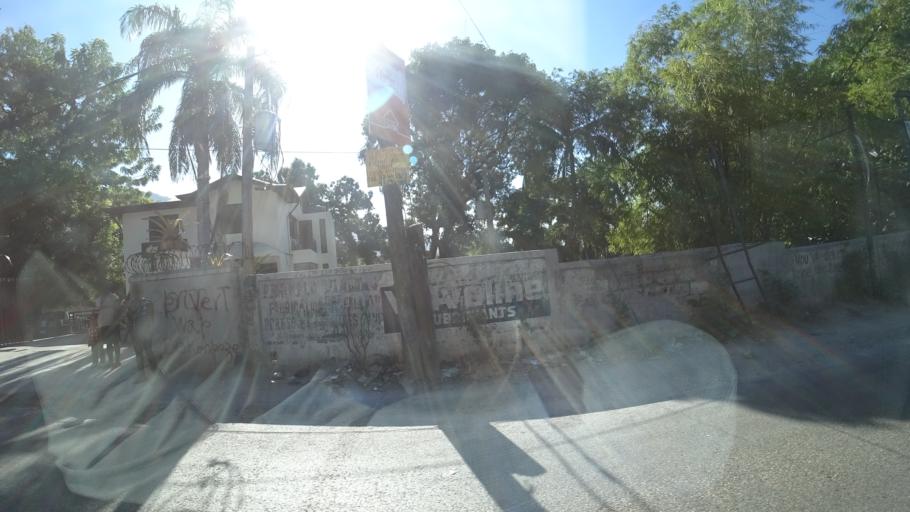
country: HT
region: Ouest
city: Delmas 73
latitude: 18.5351
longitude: -72.3107
